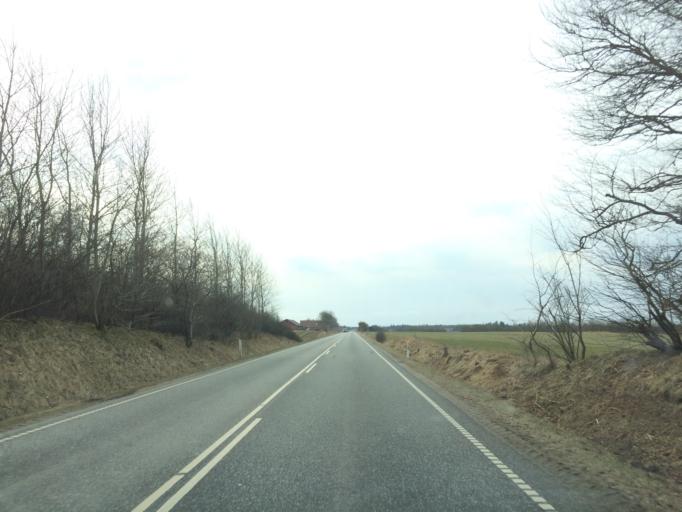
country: DK
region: Central Jutland
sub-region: Ringkobing-Skjern Kommune
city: Videbaek
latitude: 56.1045
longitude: 8.5079
